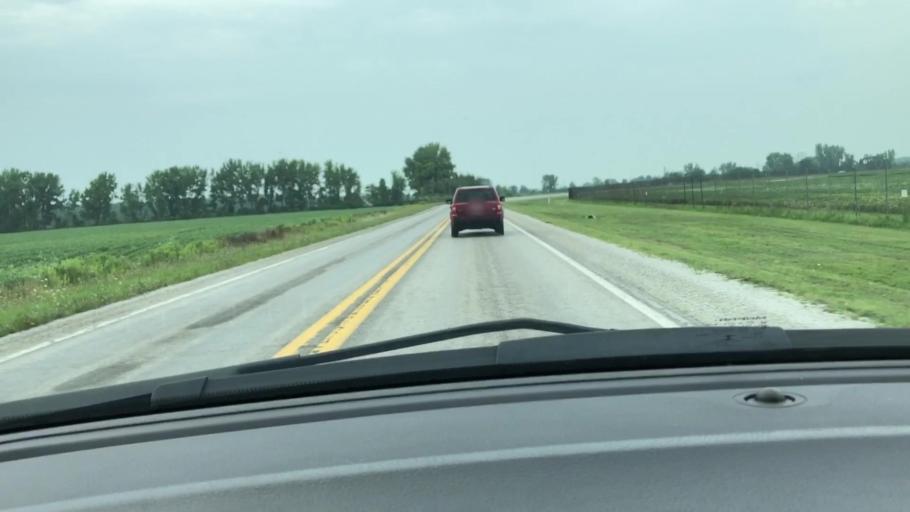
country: US
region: Michigan
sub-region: Saginaw County
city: Freeland
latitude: 43.5358
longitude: -84.0952
